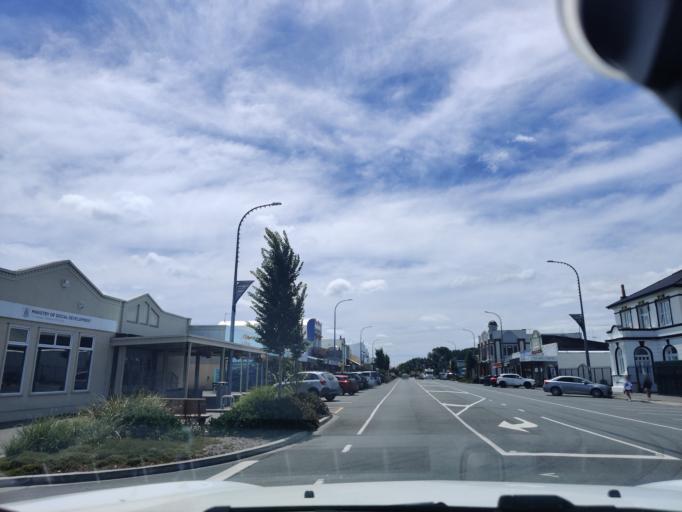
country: NZ
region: Manawatu-Wanganui
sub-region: Horowhenua District
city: Foxton
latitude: -40.4736
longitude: 175.2817
